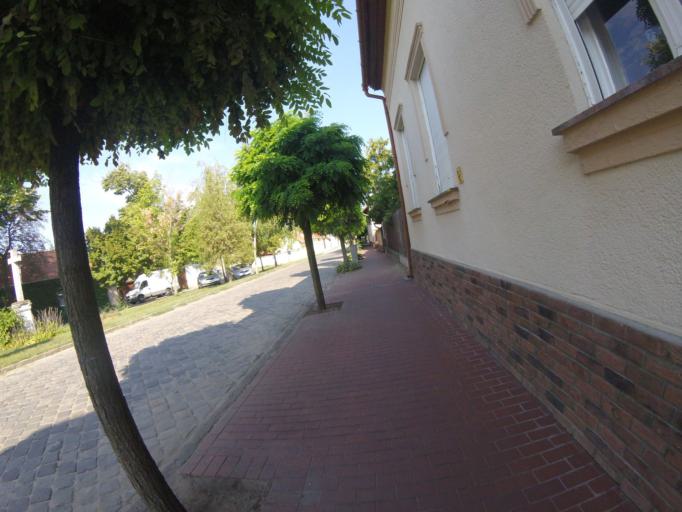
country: HU
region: Tolna
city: Dunafoldvar
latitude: 46.8116
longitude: 18.9234
